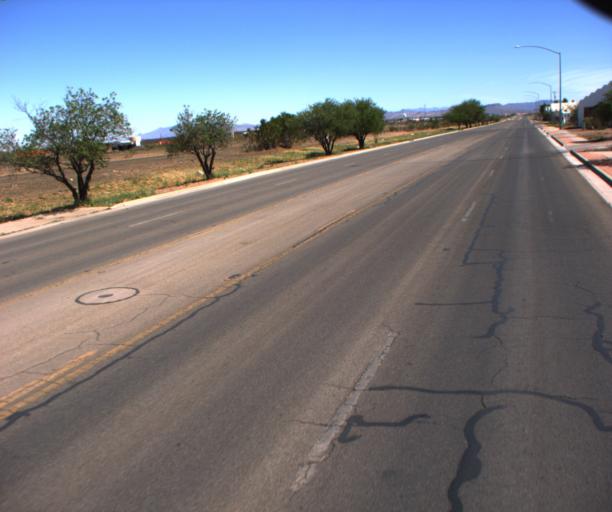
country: US
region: Arizona
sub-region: Cochise County
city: Douglas
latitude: 31.3536
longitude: -109.5516
